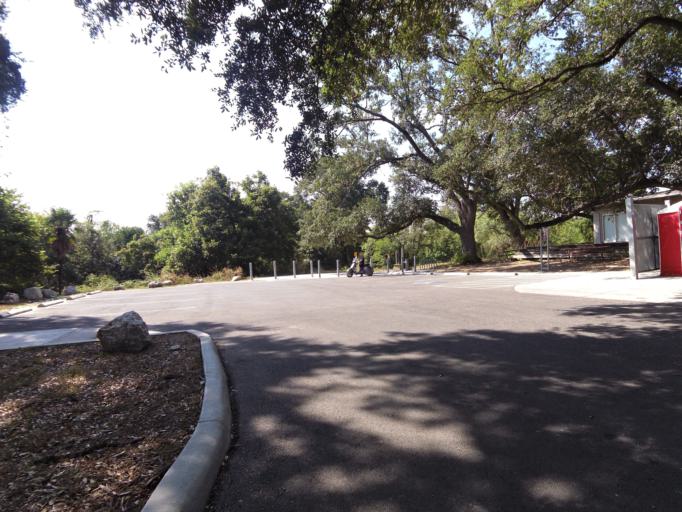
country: US
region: Texas
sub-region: Bexar County
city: Terrell Hills
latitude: 29.4526
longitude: -98.4236
